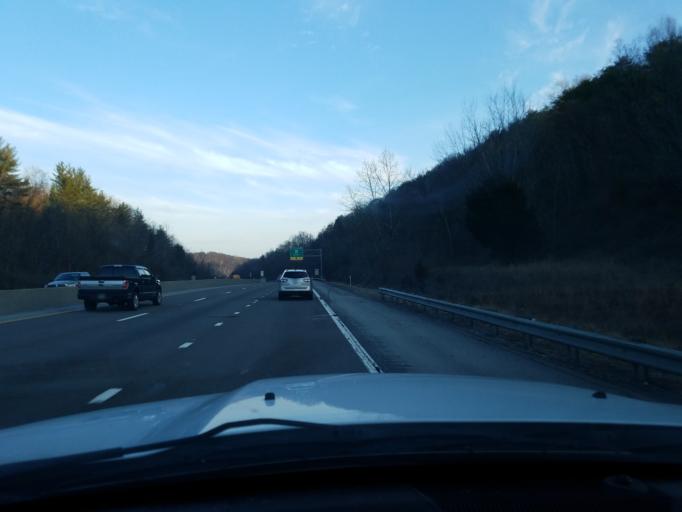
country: US
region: West Virginia
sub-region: Kanawha County
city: Nitro
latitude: 38.4354
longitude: -81.8271
